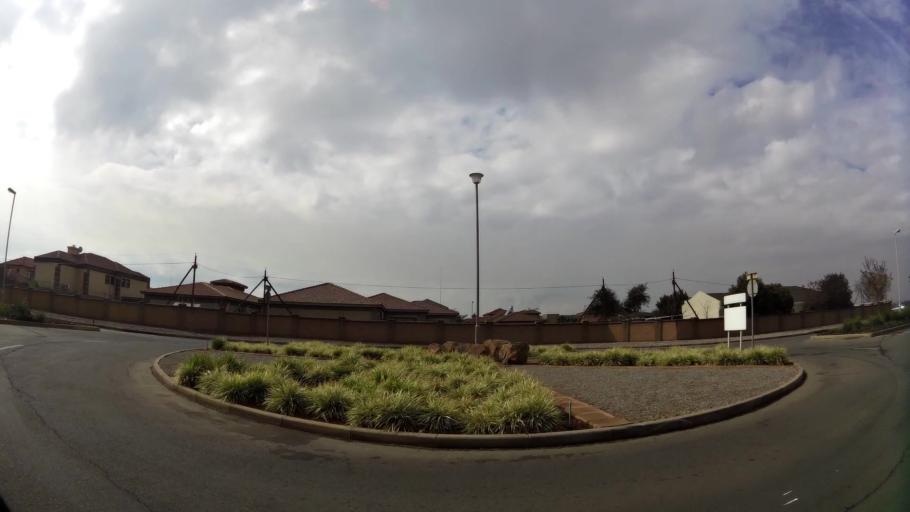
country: ZA
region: Gauteng
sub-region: Sedibeng District Municipality
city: Vanderbijlpark
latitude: -26.7282
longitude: 27.8660
